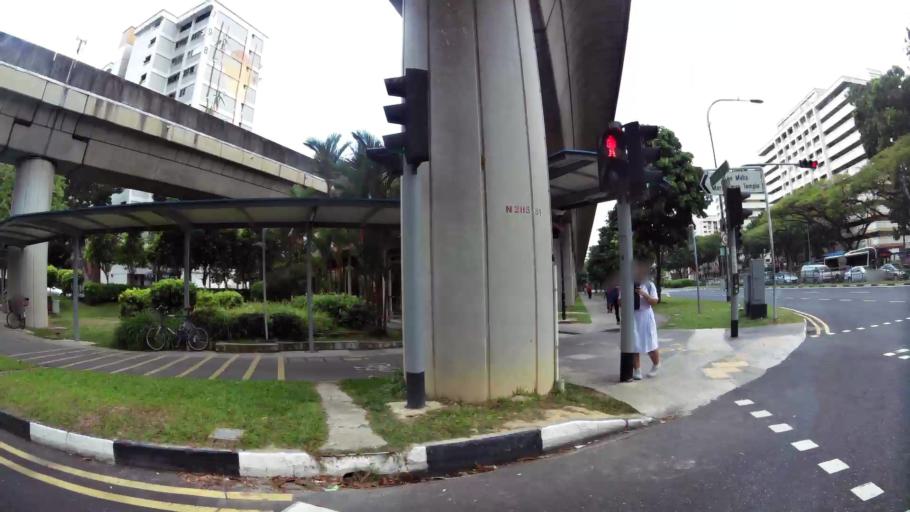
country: MY
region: Johor
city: Kampung Pasir Gudang Baru
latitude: 1.4184
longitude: 103.8337
